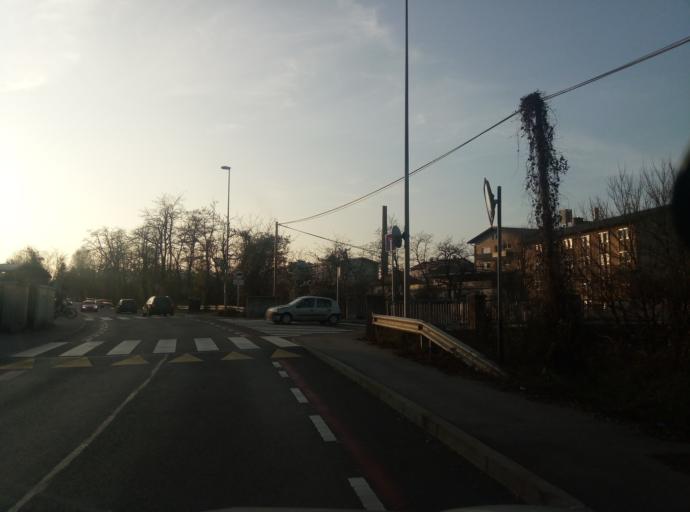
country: SI
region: Ljubljana
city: Ljubljana
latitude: 46.0479
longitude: 14.5291
